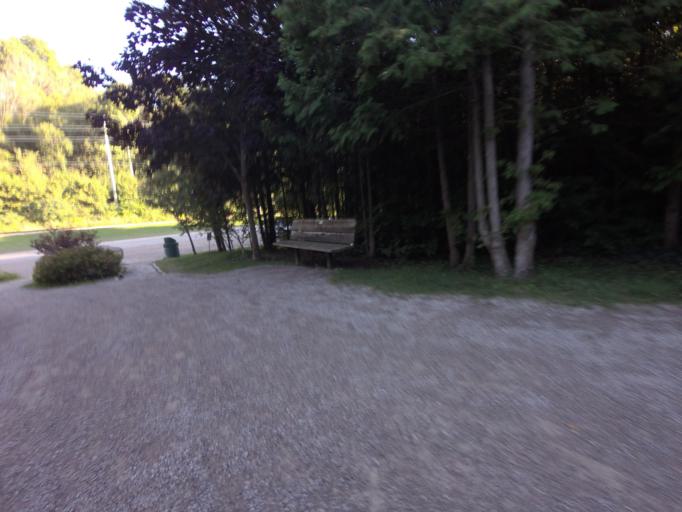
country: CA
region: Ontario
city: Goderich
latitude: 43.7483
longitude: -81.7150
